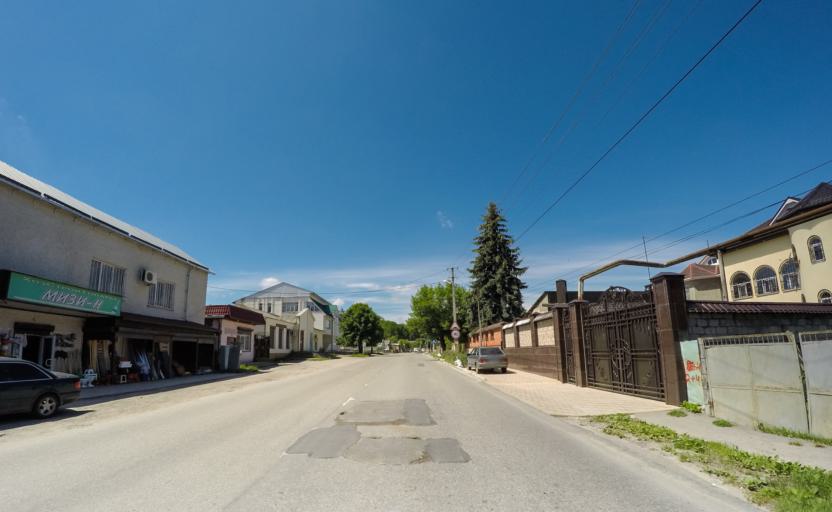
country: RU
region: Kabardino-Balkariya
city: Belaya Rechka
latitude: 43.4405
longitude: 43.5814
